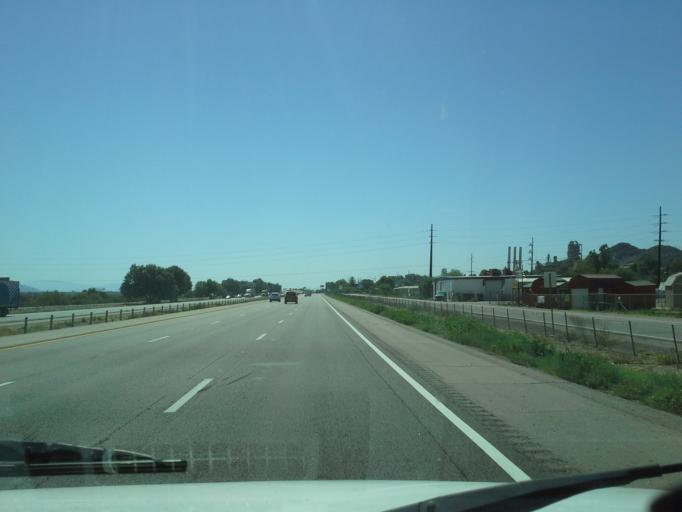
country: US
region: Arizona
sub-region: Pima County
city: Marana
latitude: 32.4187
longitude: -111.1562
